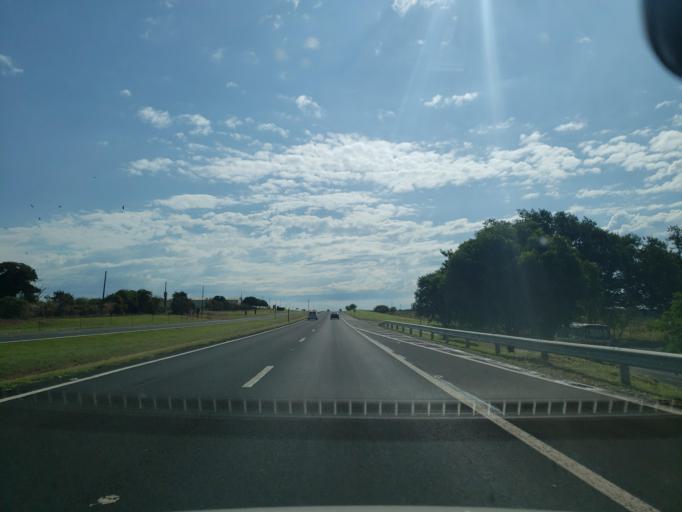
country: BR
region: Sao Paulo
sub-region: Pirajui
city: Pirajui
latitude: -22.0082
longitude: -49.4235
